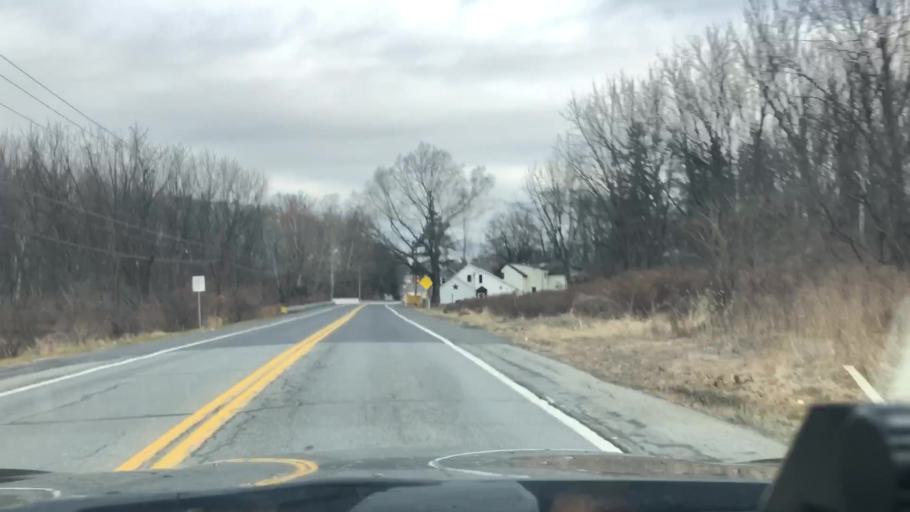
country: US
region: Pennsylvania
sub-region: Northampton County
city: Middletown
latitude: 40.6834
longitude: -75.3397
